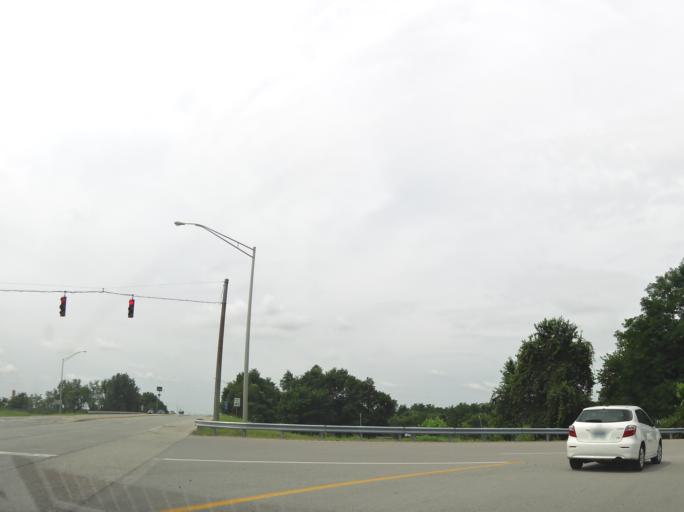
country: US
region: Kentucky
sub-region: Scott County
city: Georgetown
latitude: 38.2275
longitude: -84.5374
